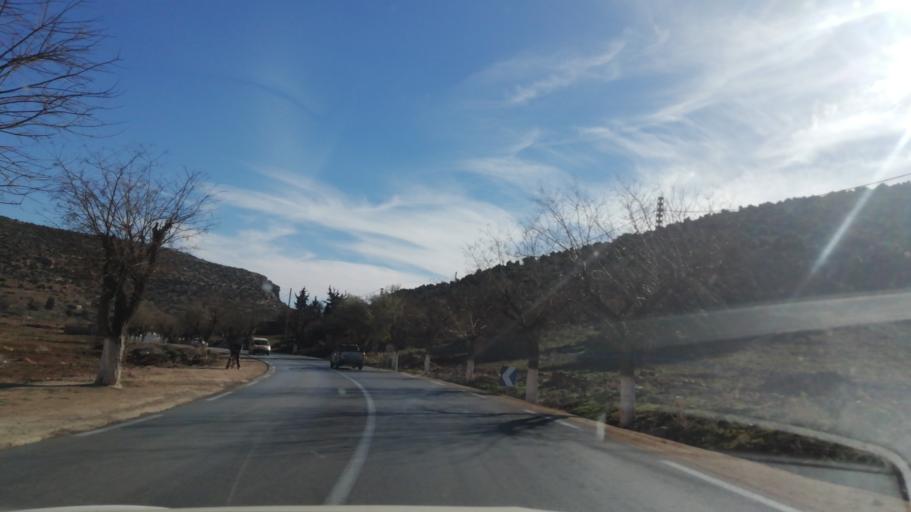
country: DZ
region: Tlemcen
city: Sebdou
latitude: 34.7000
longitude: -1.3154
